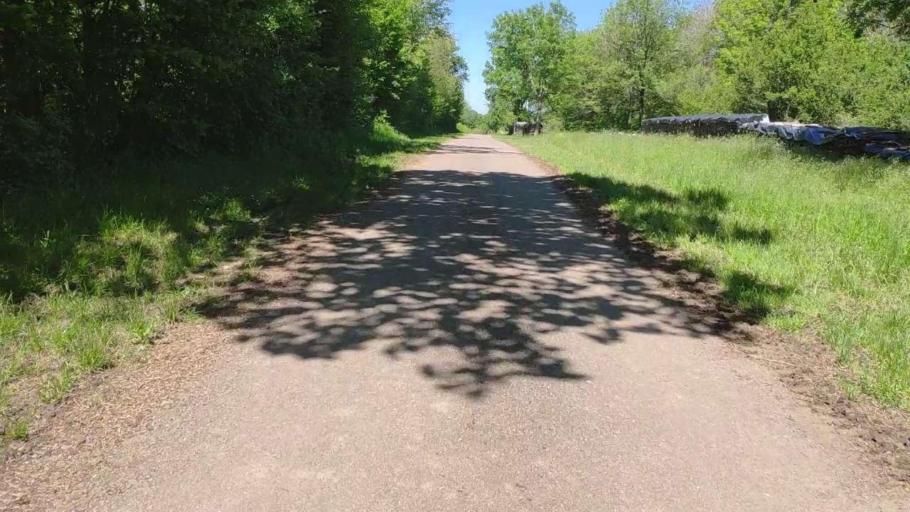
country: FR
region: Franche-Comte
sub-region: Departement du Jura
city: Perrigny
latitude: 46.7131
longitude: 5.6558
